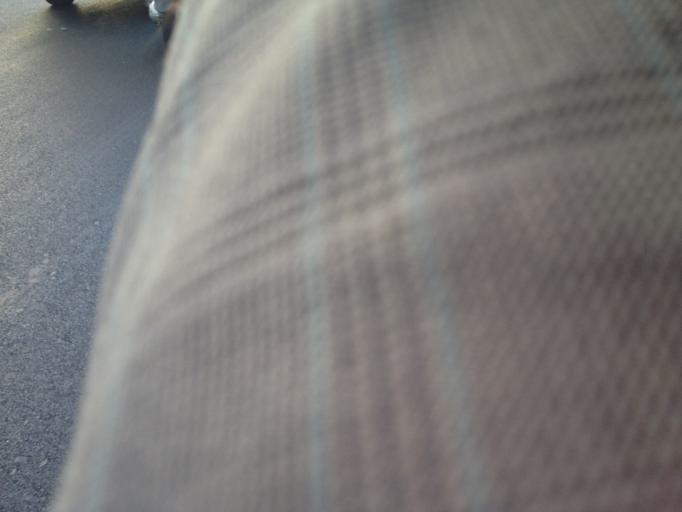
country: TH
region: Bangkok
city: Bangkok
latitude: 13.7595
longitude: 100.5023
